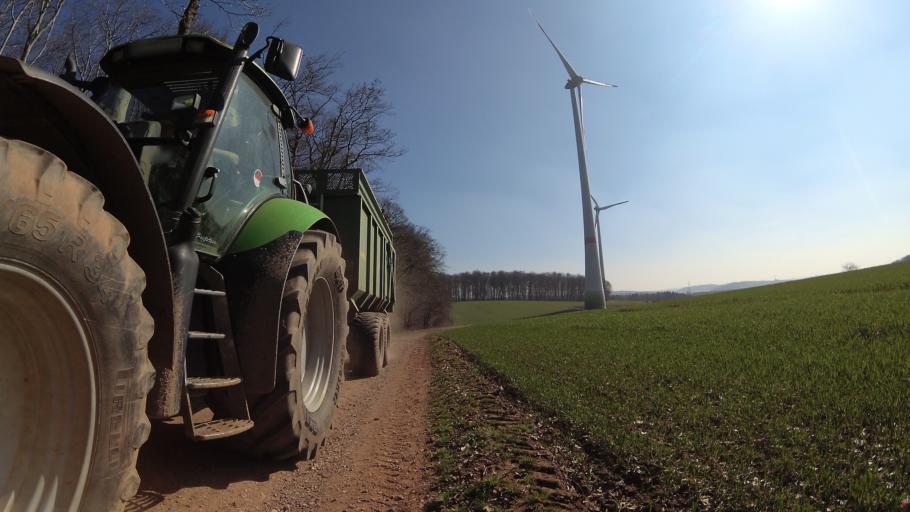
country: DE
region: Saarland
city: Eppelborn
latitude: 49.4315
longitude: 6.9781
